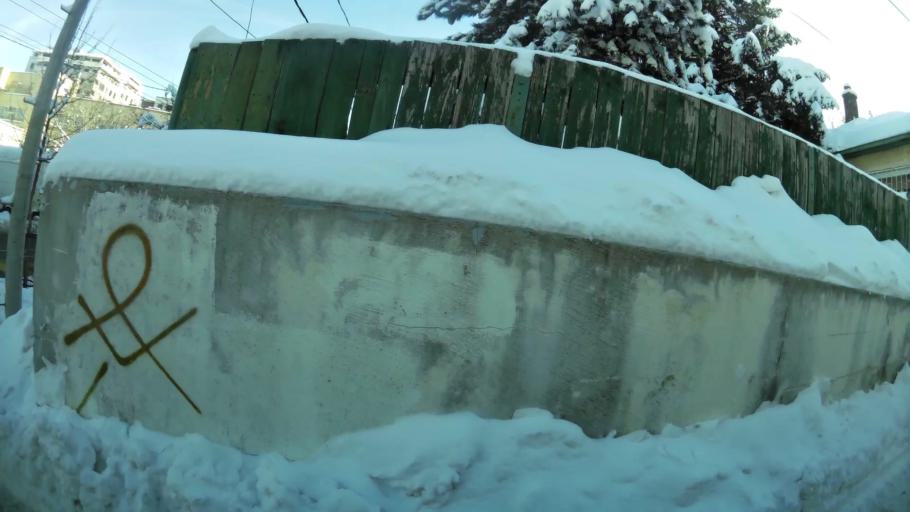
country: RS
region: Central Serbia
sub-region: Belgrade
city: Vracar
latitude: 44.7912
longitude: 20.4964
